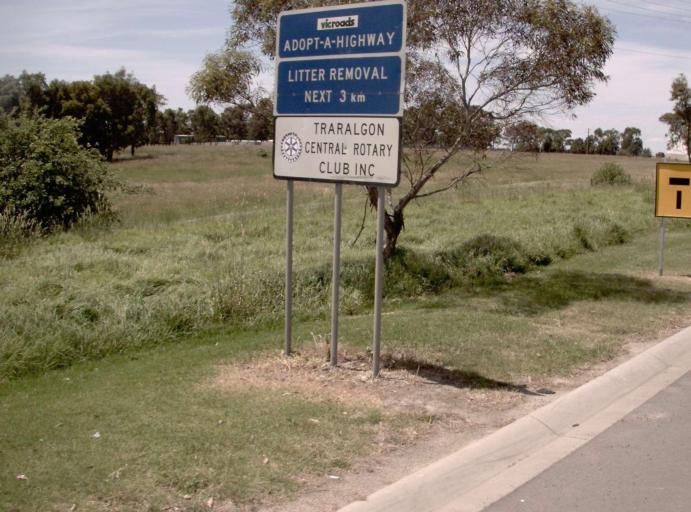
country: AU
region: Victoria
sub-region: Latrobe
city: Traralgon
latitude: -38.1887
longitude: 146.5728
